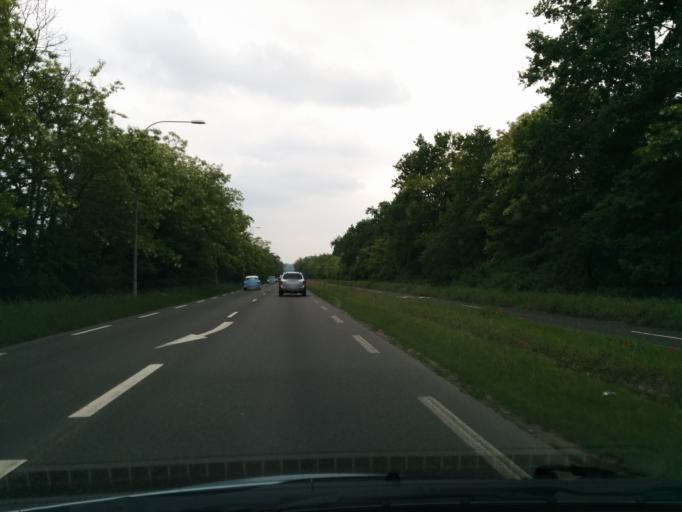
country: FR
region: Ile-de-France
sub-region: Departement des Yvelines
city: Mezy-sur-Seine
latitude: 48.9816
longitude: 1.8894
